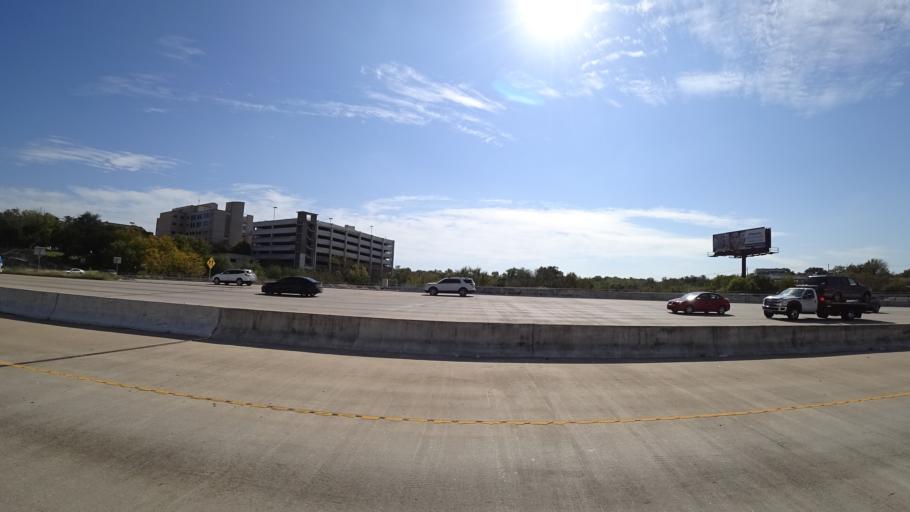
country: US
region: Texas
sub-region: Travis County
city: Rollingwood
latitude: 30.2278
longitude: -97.7761
